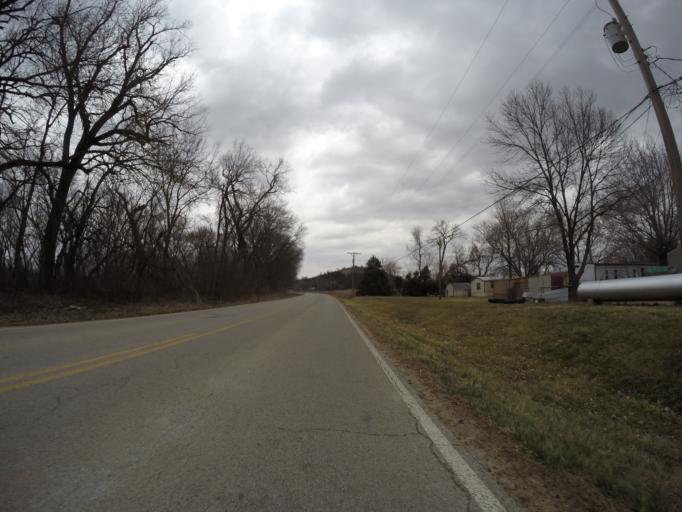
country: US
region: Kansas
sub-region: Riley County
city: Manhattan
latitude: 39.2470
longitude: -96.5702
